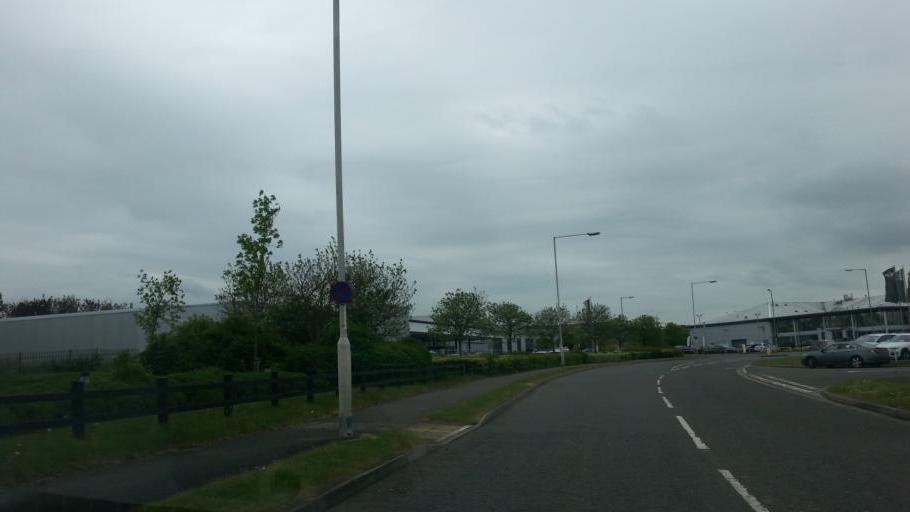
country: GB
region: England
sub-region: Peterborough
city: Marholm
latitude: 52.6174
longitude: -0.2904
